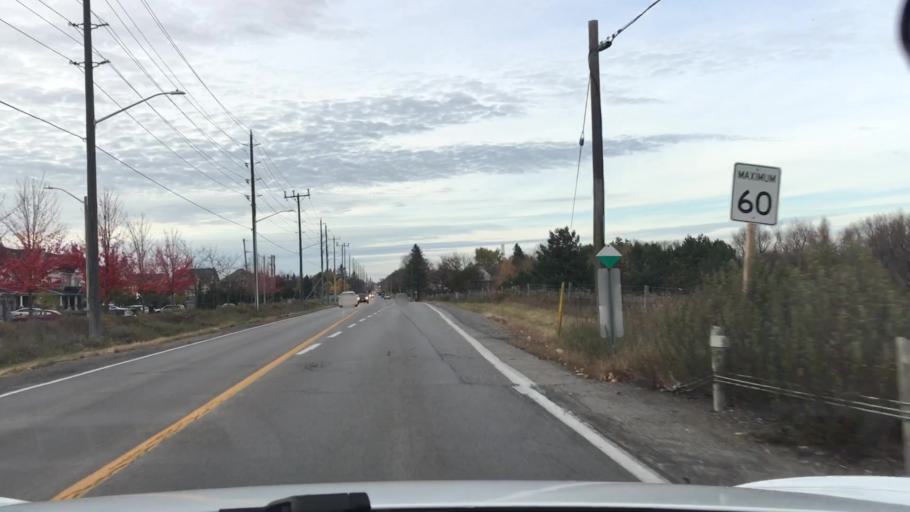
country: CA
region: Ontario
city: Oshawa
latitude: 43.9379
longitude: -78.8271
